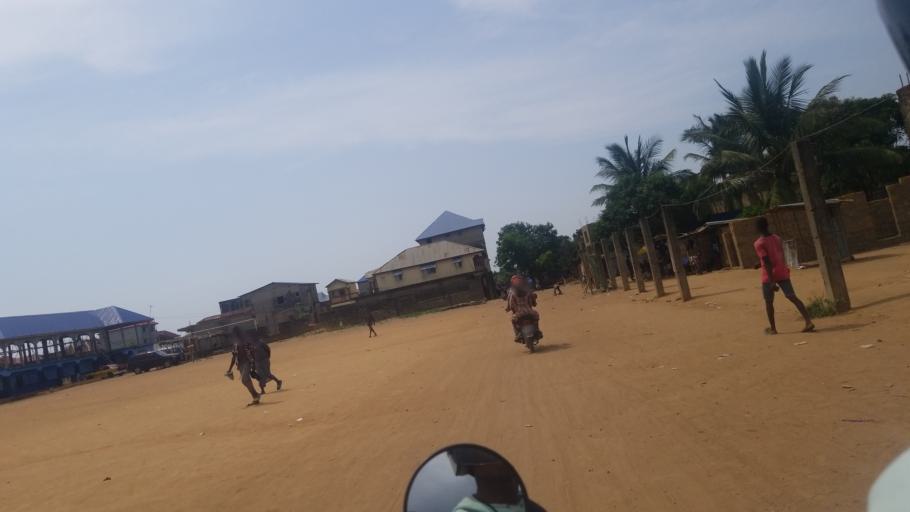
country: SL
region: Western Area
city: Waterloo
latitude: 8.3273
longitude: -13.0487
